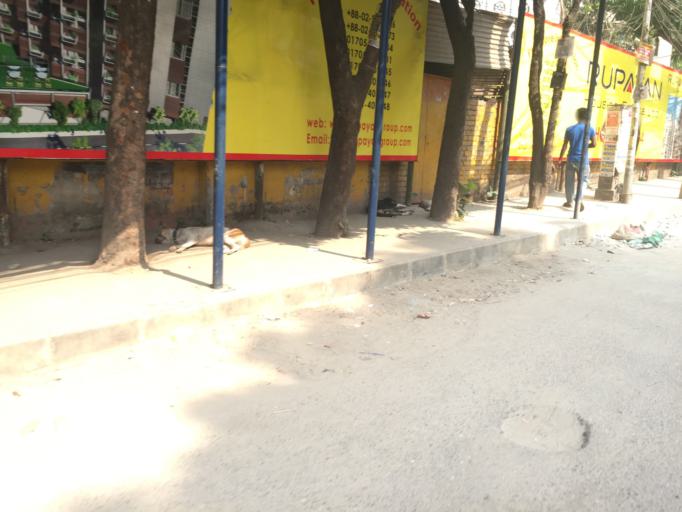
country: BD
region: Dhaka
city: Paltan
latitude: 23.7444
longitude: 90.4073
